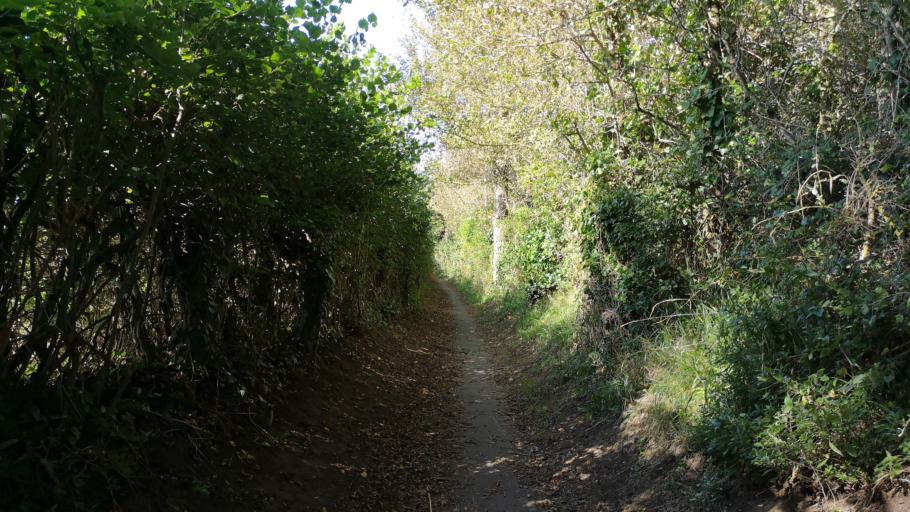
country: GB
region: England
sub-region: Isle of Wight
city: Totland
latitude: 50.6771
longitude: -1.5244
